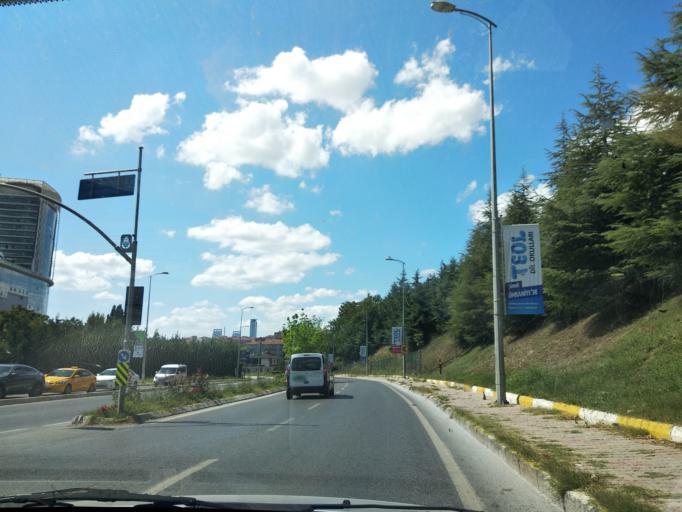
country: TR
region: Istanbul
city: Umraniye
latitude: 41.0069
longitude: 29.1091
